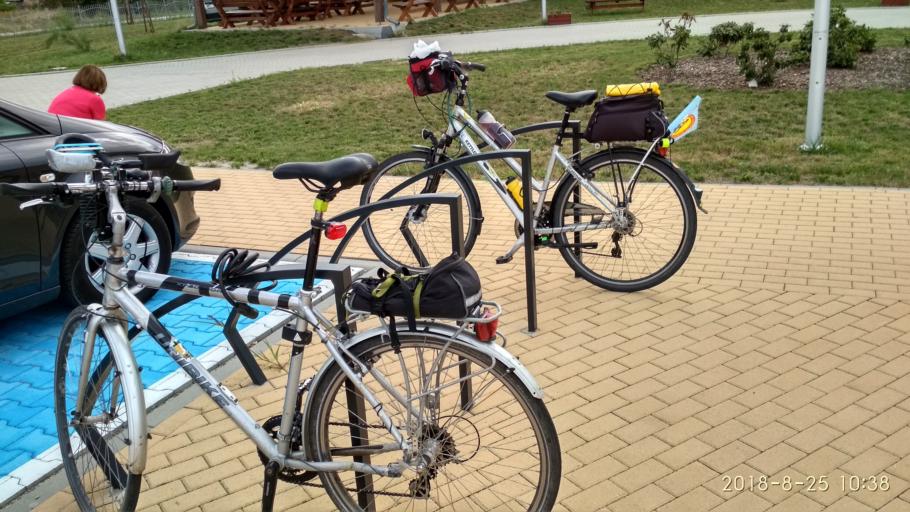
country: PL
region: Lubusz
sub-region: Powiat zielonogorski
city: Zabor
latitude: 51.9507
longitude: 15.7097
